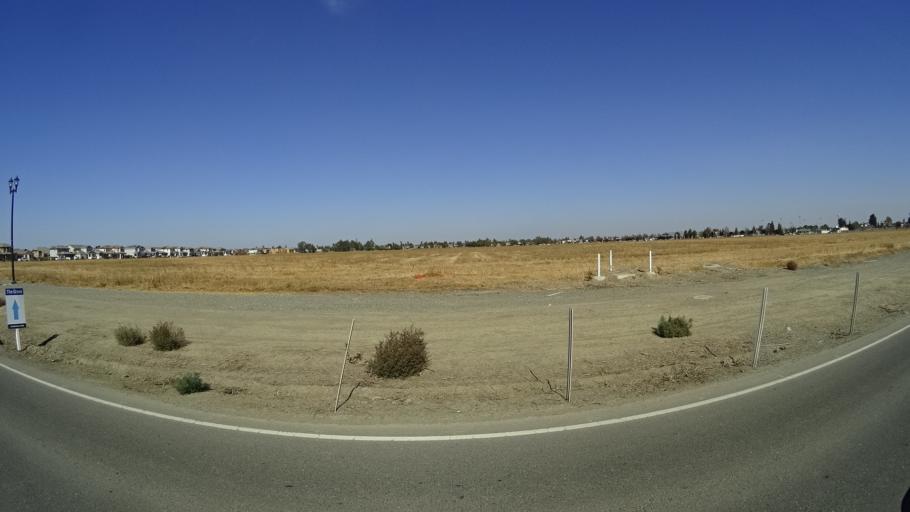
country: US
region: California
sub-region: Yolo County
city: Woodland
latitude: 38.6552
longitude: -121.7453
